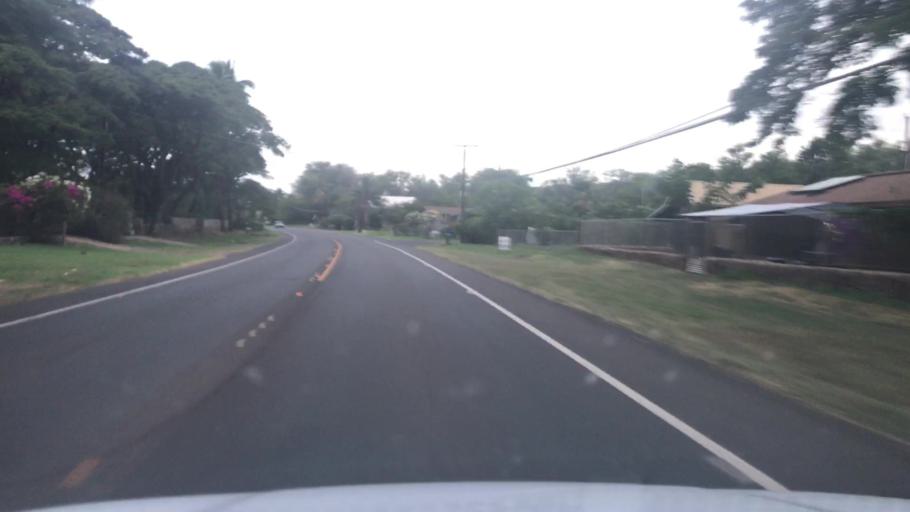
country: US
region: Hawaii
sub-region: Maui County
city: Kaunakakai
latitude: 21.0665
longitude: -156.9517
